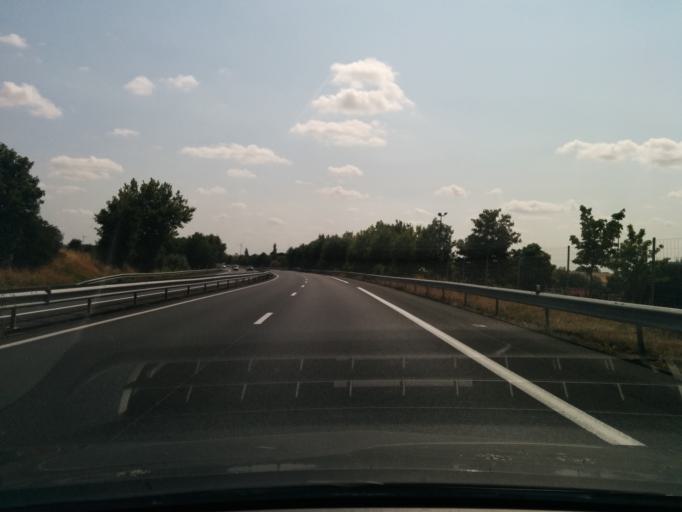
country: FR
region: Centre
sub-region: Departement de l'Indre
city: Vatan
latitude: 47.0489
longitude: 1.8004
